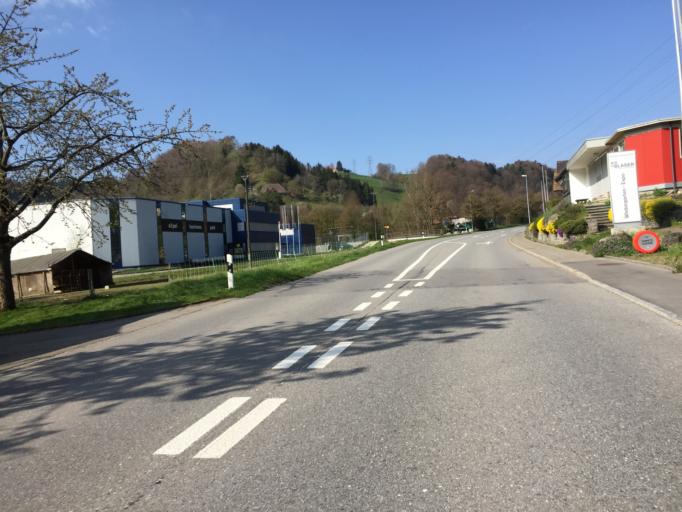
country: CH
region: Bern
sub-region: Bern-Mittelland District
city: Bariswil
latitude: 46.9990
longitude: 7.5400
